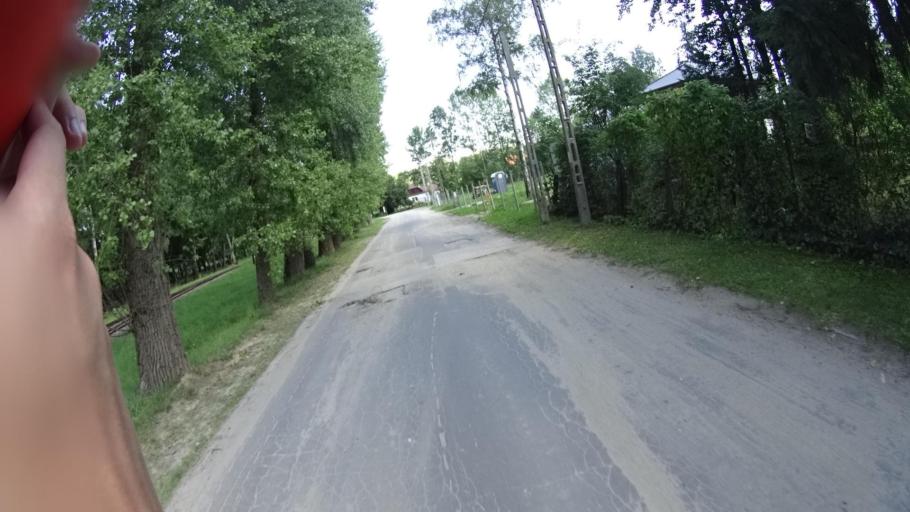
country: PL
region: Masovian Voivodeship
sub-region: Powiat piaseczynski
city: Prazmow
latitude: 52.0049
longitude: 20.9120
